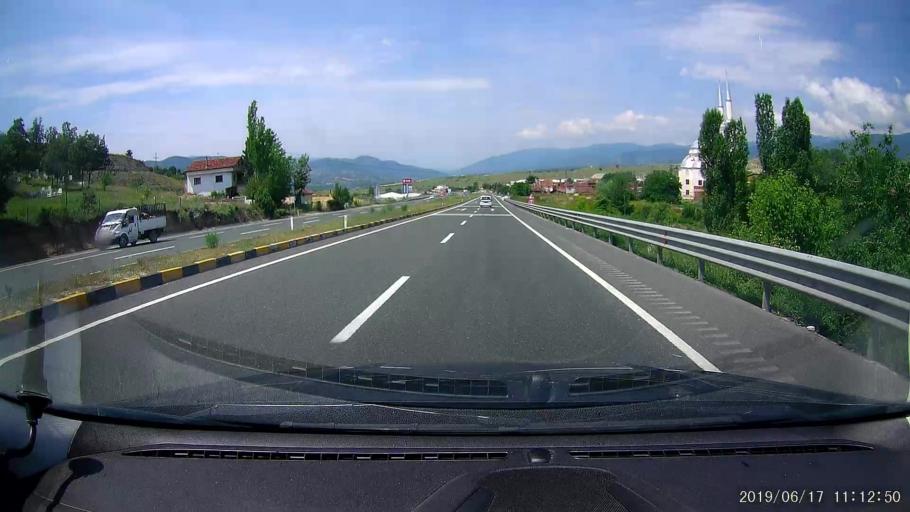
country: TR
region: Kastamonu
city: Tosya
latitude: 40.9686
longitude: 33.9862
